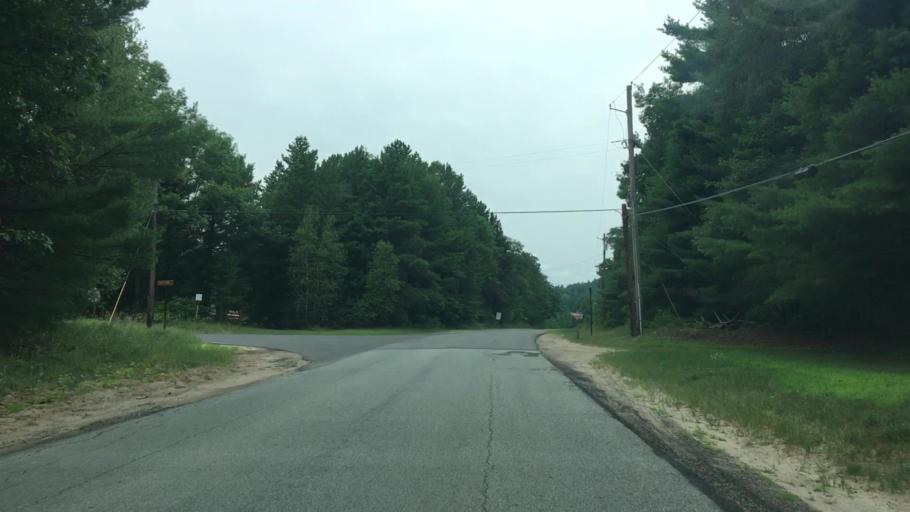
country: US
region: New York
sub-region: Essex County
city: Keeseville
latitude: 44.4575
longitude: -73.5810
